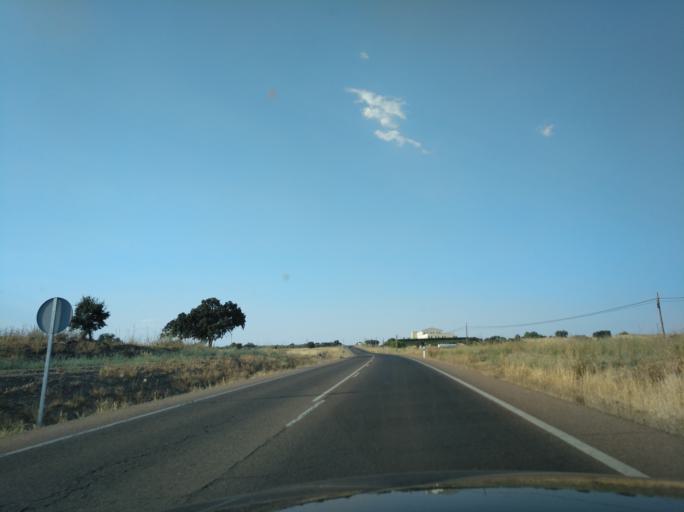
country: ES
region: Extremadura
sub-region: Provincia de Badajoz
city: Olivenza
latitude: 38.7045
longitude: -7.0871
